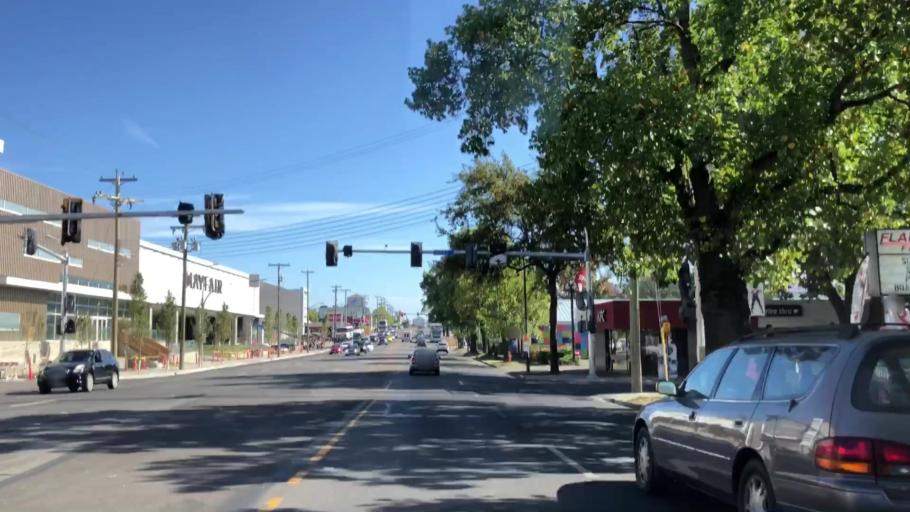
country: CA
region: British Columbia
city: Victoria
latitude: 48.4468
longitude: -123.3719
